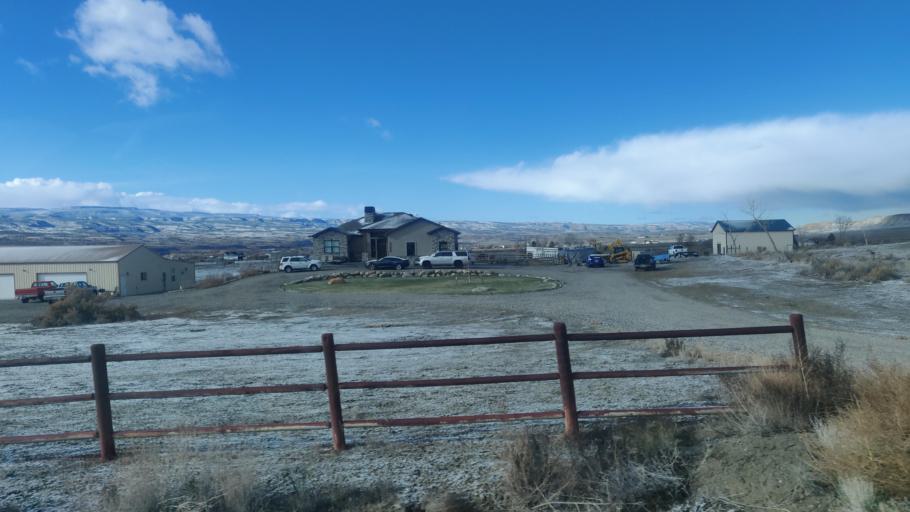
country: US
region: Colorado
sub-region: Mesa County
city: Clifton
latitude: 38.9962
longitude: -108.4249
